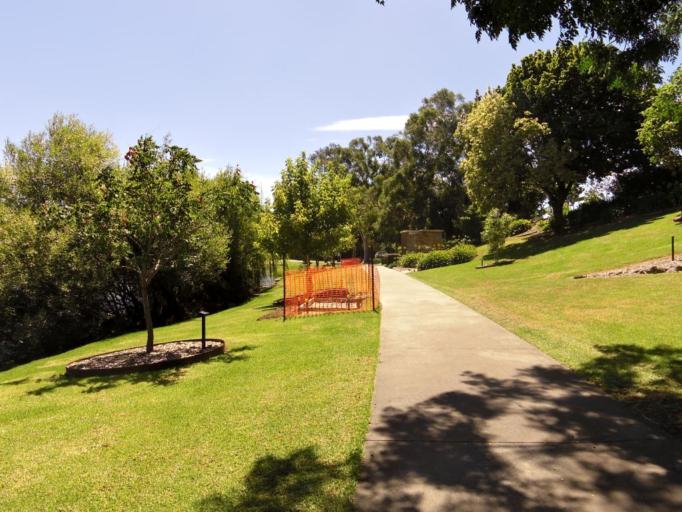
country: AU
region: Victoria
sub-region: Wodonga
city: Wodonga
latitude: -36.1127
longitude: 146.8914
